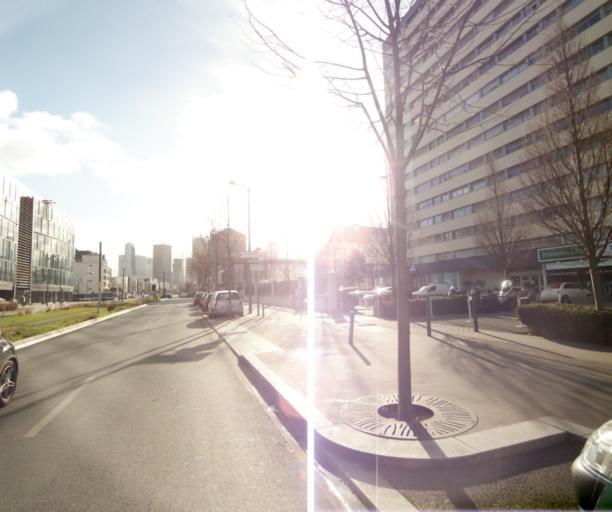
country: FR
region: Ile-de-France
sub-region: Departement des Hauts-de-Seine
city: La Garenne-Colombes
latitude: 48.9058
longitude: 2.2390
